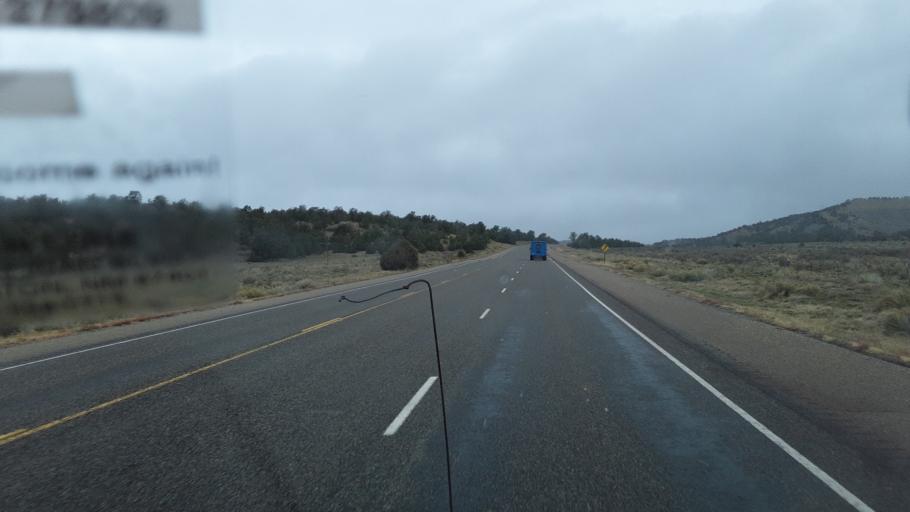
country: US
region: New Mexico
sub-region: Rio Arriba County
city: Tierra Amarilla
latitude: 36.4483
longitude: -106.4758
